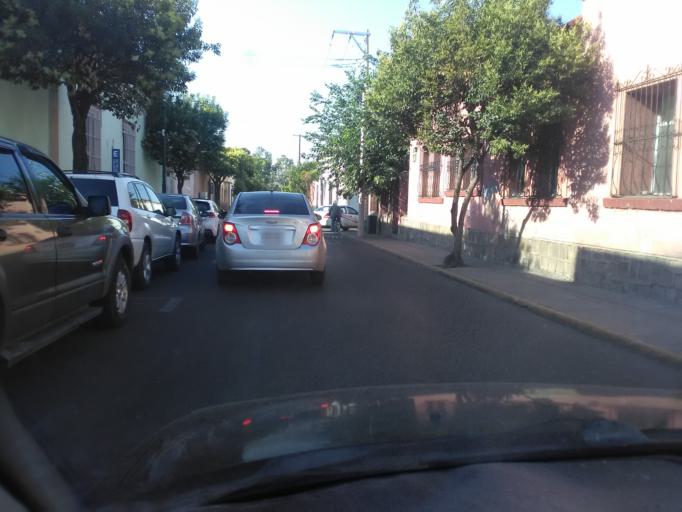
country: MX
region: Durango
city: Victoria de Durango
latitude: 24.0230
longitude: -104.6741
